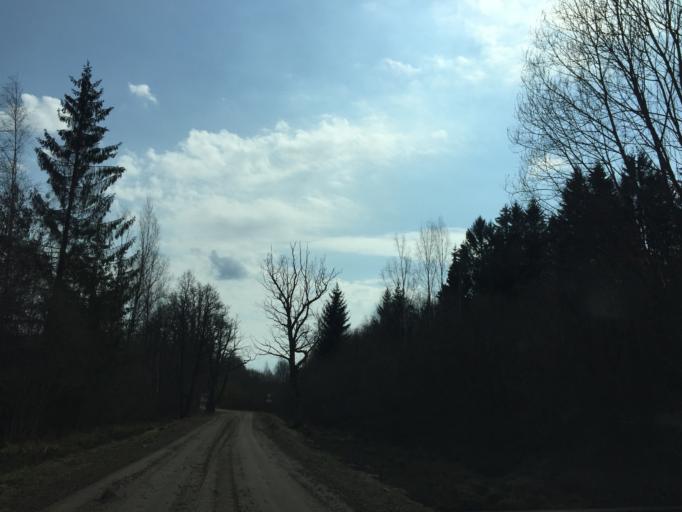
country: LV
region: Aluksnes Rajons
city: Aluksne
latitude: 57.5601
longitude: 26.9125
